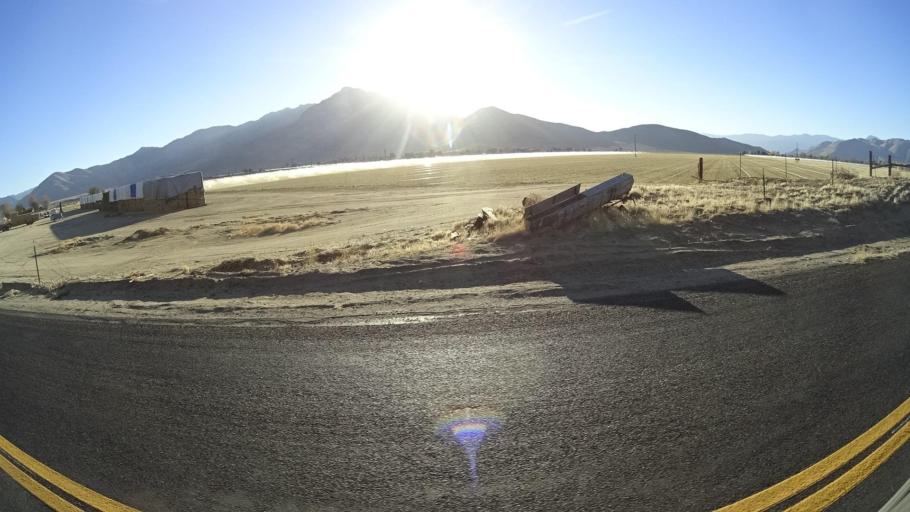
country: US
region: California
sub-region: Kern County
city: Weldon
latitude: 35.6592
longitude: -118.2560
